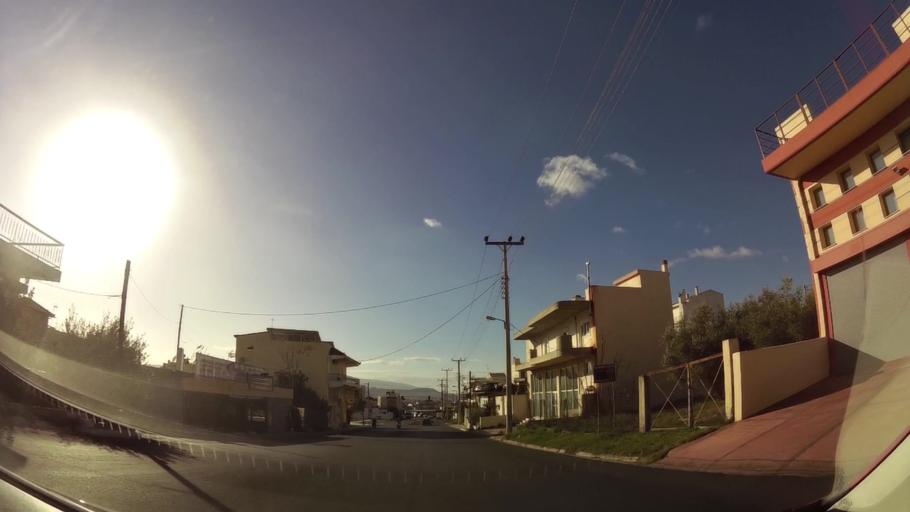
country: GR
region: Attica
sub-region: Nomarchia Anatolikis Attikis
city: Acharnes
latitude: 38.0727
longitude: 23.7437
